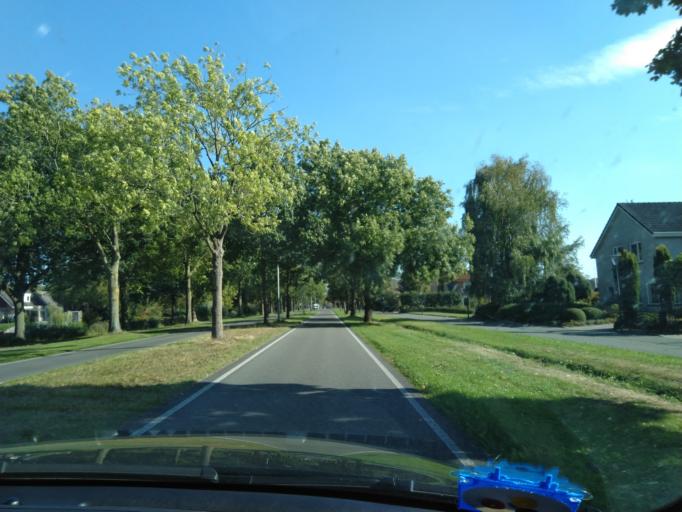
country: NL
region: Groningen
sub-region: Gemeente Veendam
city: Veendam
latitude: 53.0880
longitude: 6.8560
